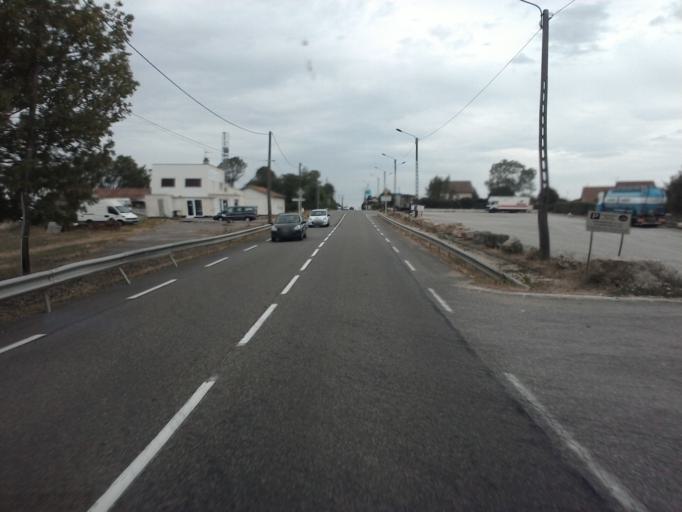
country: FR
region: Lorraine
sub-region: Departement de Meurthe-et-Moselle
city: Colombey-les-Belles
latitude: 48.5213
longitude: 5.8924
